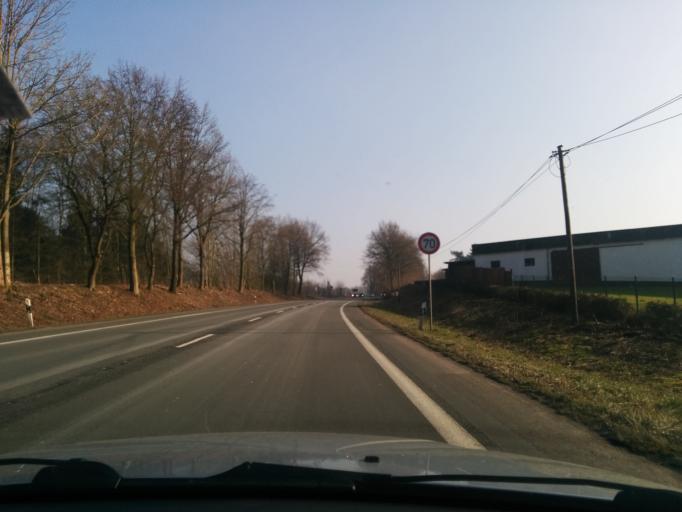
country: DE
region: North Rhine-Westphalia
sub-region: Regierungsbezirk Detmold
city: Dorentrup
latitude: 52.0046
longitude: 8.9649
